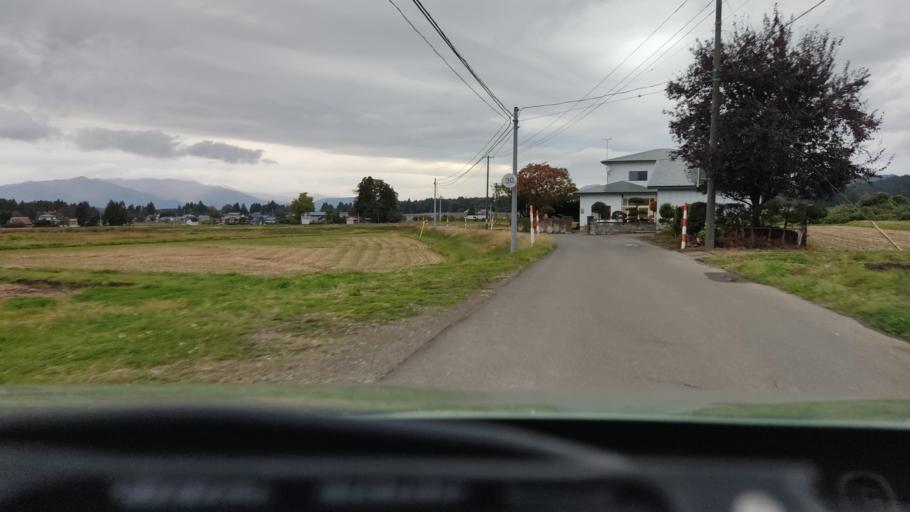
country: JP
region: Akita
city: Kakunodatemachi
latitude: 39.5628
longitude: 140.6109
